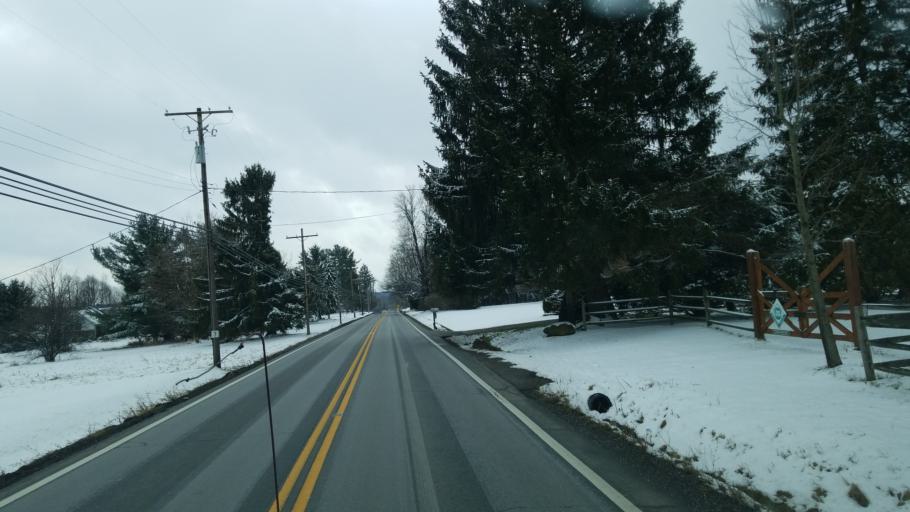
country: US
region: Ohio
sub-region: Geauga County
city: Burton
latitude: 41.4488
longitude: -81.1359
